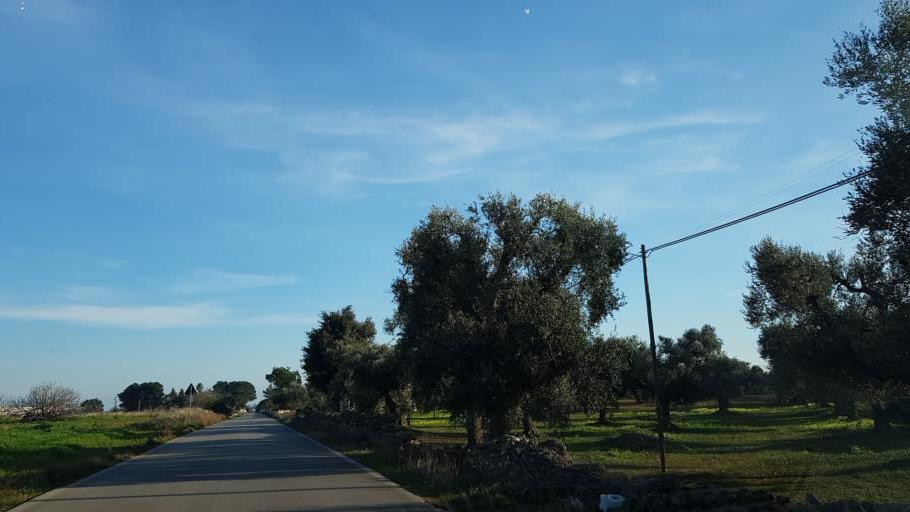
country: IT
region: Apulia
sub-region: Provincia di Brindisi
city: San Vito dei Normanni
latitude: 40.6842
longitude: 17.7671
